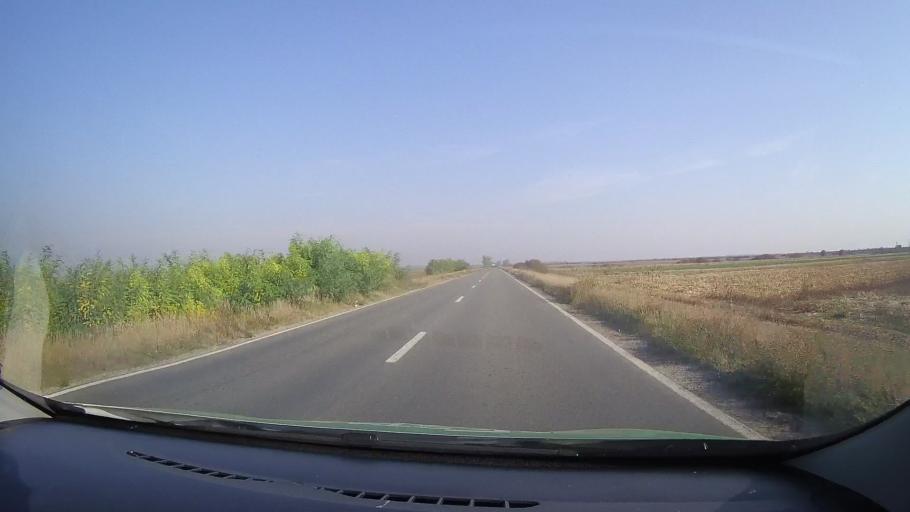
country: RO
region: Arad
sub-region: Comuna Pilu
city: Pilu
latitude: 46.5874
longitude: 21.3452
